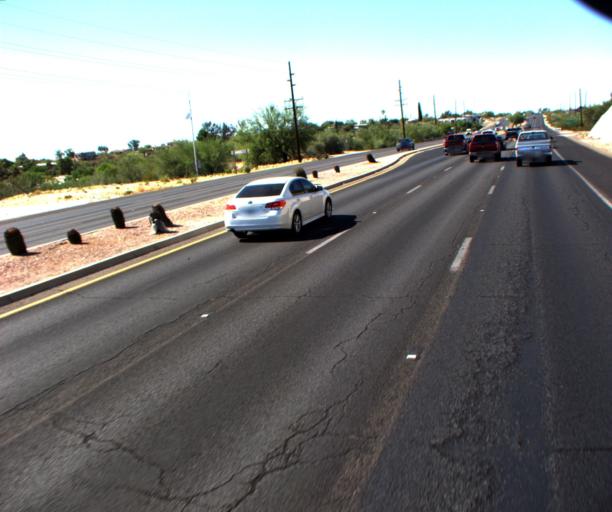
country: US
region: Arizona
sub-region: Pima County
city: Casas Adobes
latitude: 32.3013
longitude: -110.9783
